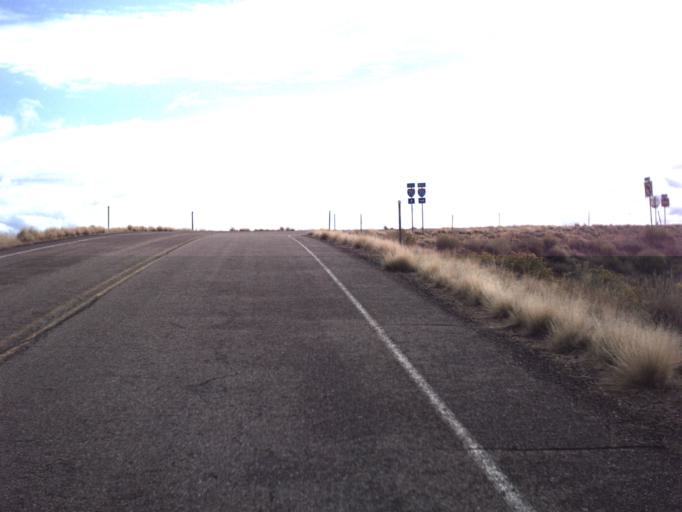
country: US
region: Utah
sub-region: Grand County
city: Moab
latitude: 38.9223
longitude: -109.9369
